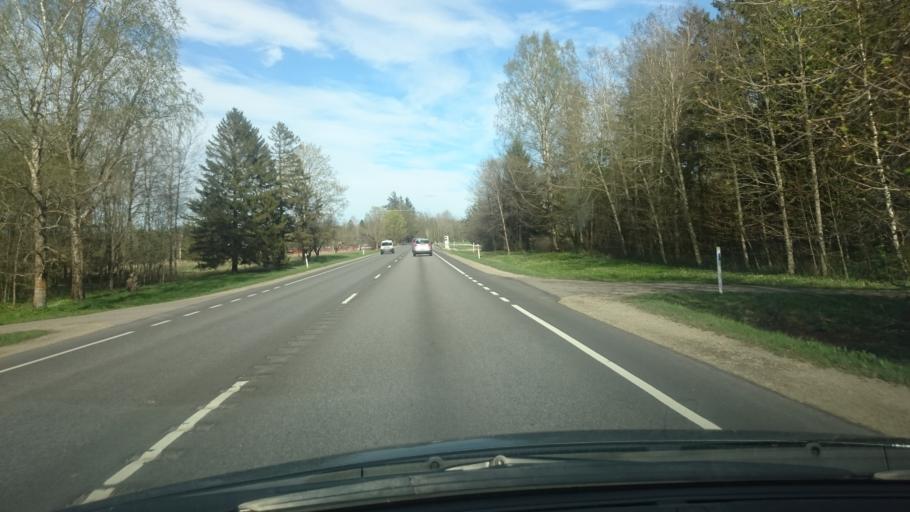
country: EE
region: Ida-Virumaa
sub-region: Toila vald
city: Voka
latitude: 59.3936
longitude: 27.6280
